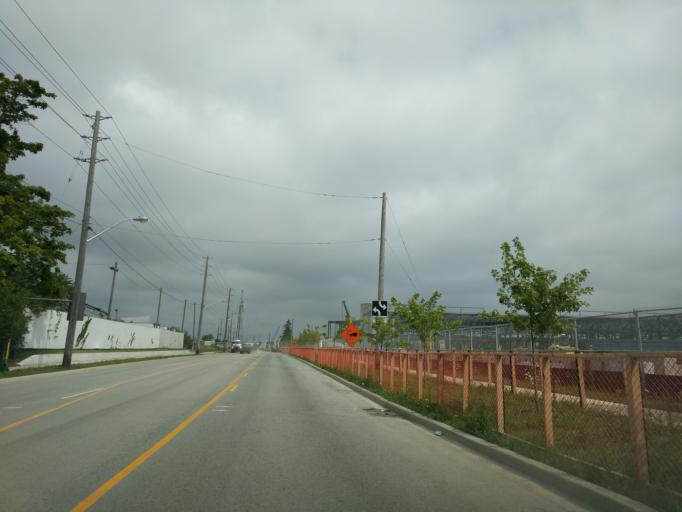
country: CA
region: Ontario
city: Scarborough
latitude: 43.8135
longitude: -79.2996
